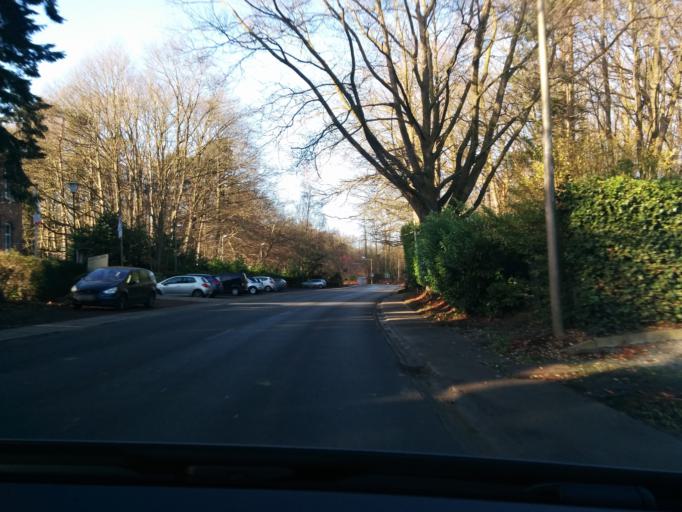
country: BE
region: Flanders
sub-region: Provincie Vlaams-Brabant
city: Beersel
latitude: 50.7548
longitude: 4.3167
